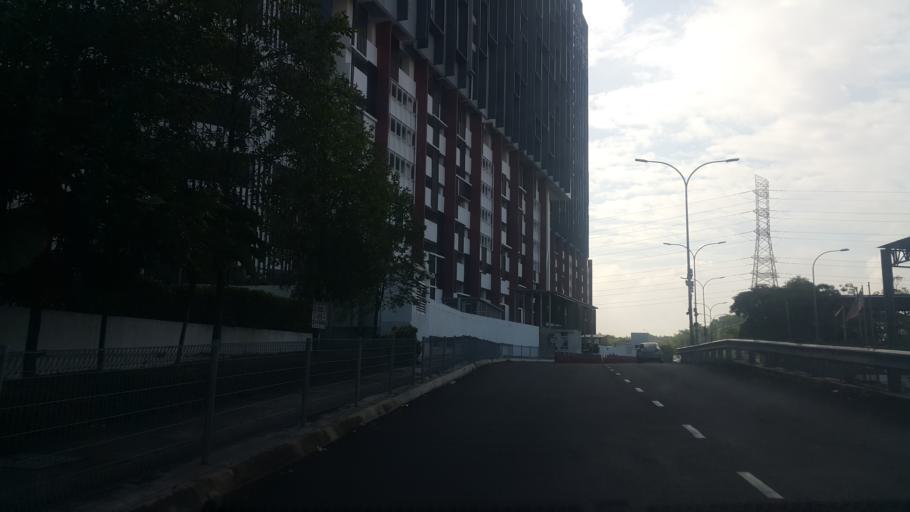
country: MY
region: Selangor
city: Klang
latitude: 2.9940
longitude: 101.4429
